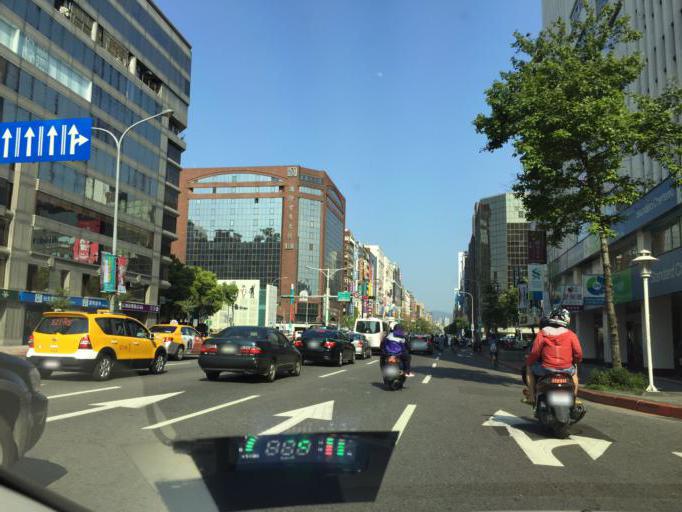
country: TW
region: Taipei
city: Taipei
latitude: 25.0415
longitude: 121.5478
